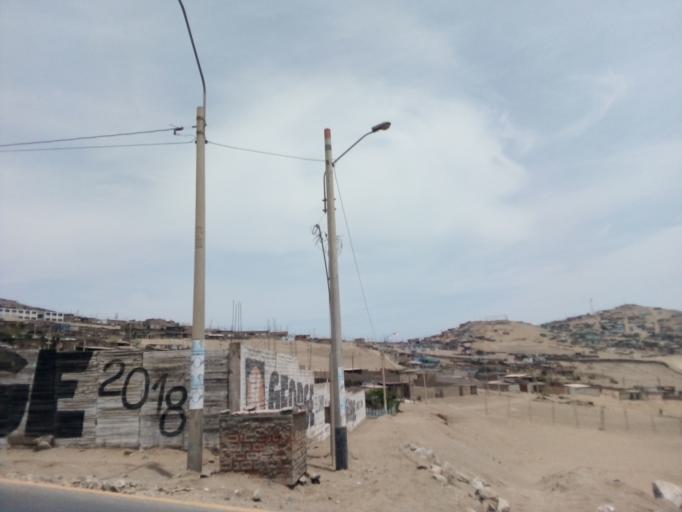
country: PE
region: Lima
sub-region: Lima
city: Santa Rosa
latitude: -11.8188
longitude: -77.1634
